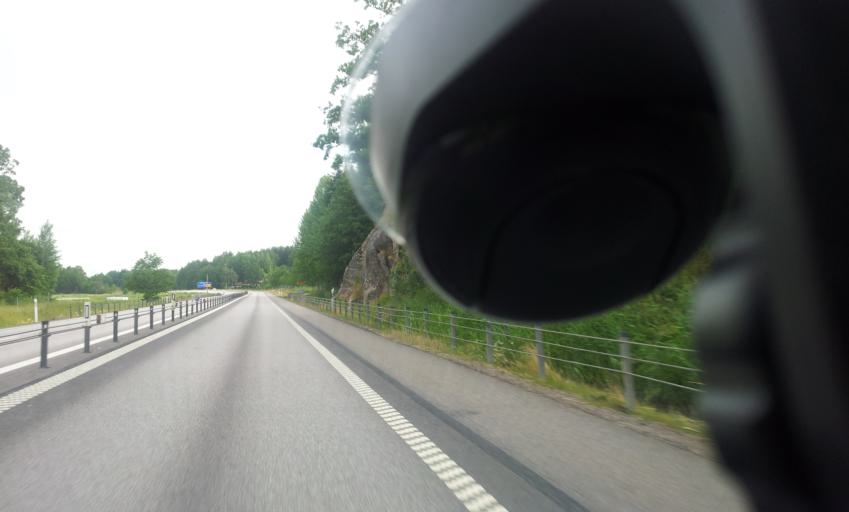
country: SE
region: OEstergoetland
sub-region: Valdemarsviks Kommun
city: Gusum
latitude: 58.3751
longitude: 16.4244
